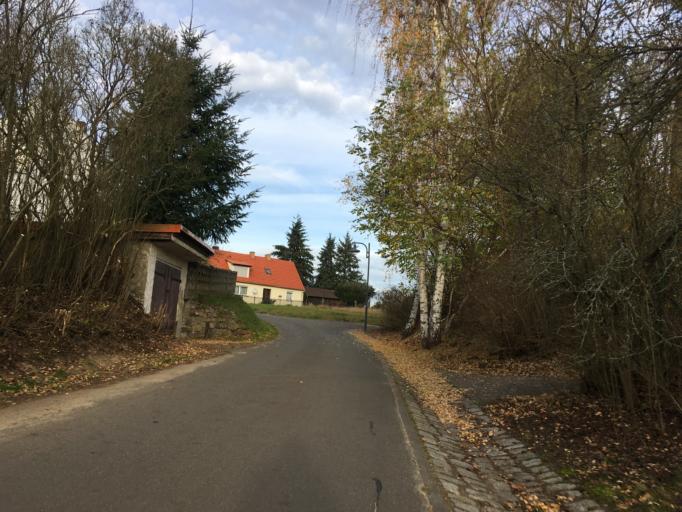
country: DE
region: Brandenburg
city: Schlepzig
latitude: 52.0341
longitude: 13.8355
